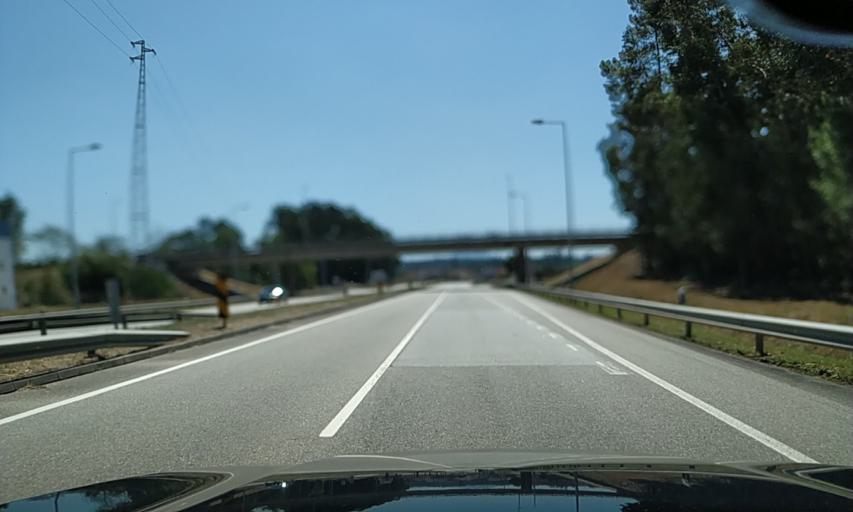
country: PT
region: Aveiro
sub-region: Agueda
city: Aguada de Cima
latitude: 40.5232
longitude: -8.4510
